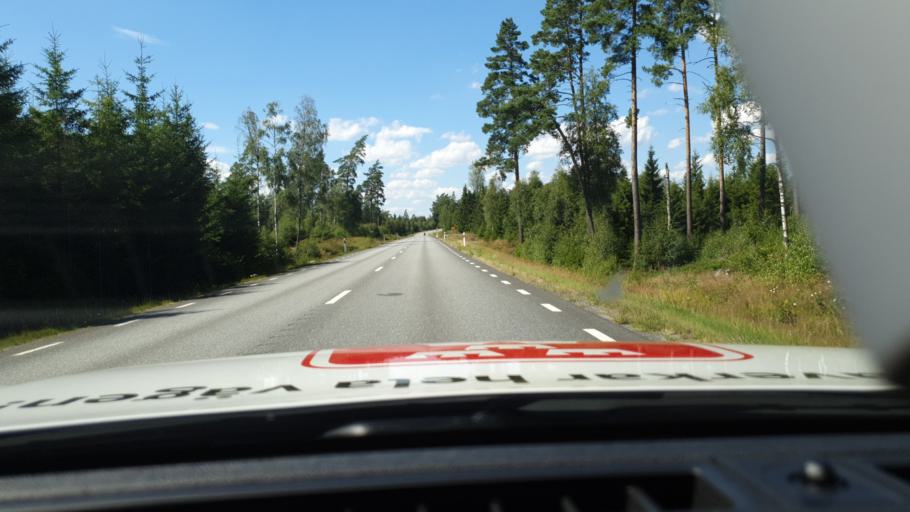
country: SE
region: Joenkoeping
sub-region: Savsjo Kommun
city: Vrigstad
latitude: 57.3882
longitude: 14.3902
